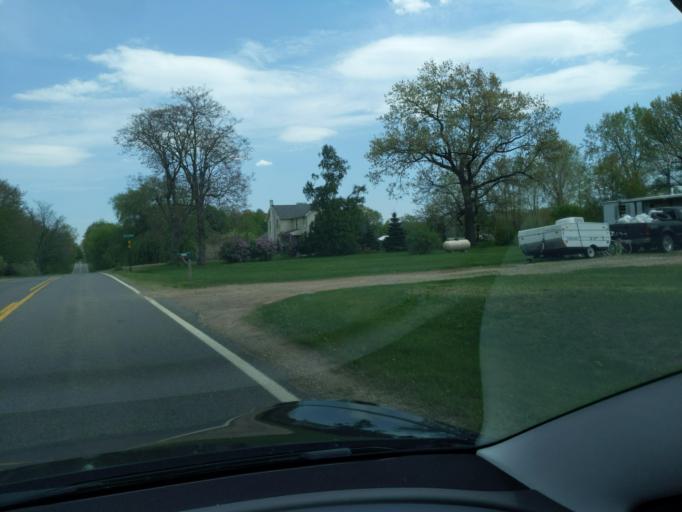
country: US
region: Michigan
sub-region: Ingham County
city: Stockbridge
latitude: 42.4832
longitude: -84.2405
